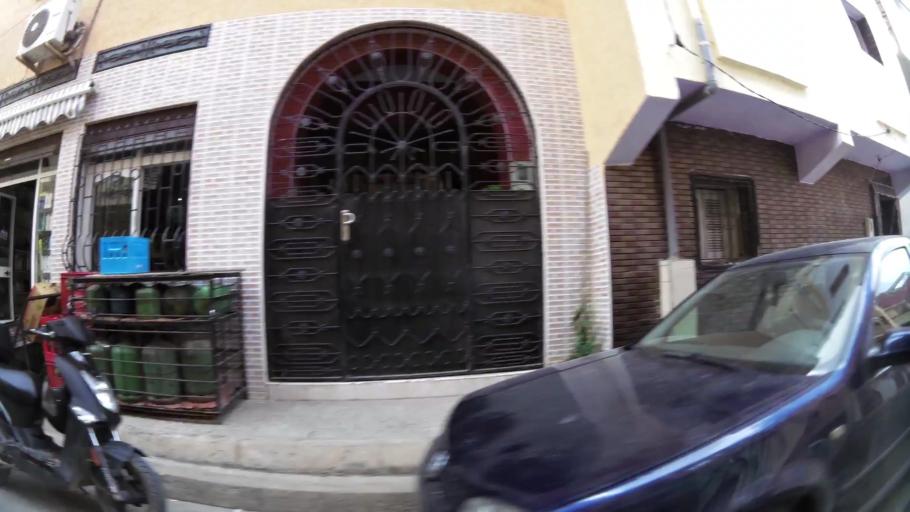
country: MA
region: Oriental
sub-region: Nador
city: Nador
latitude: 35.1693
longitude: -2.9305
